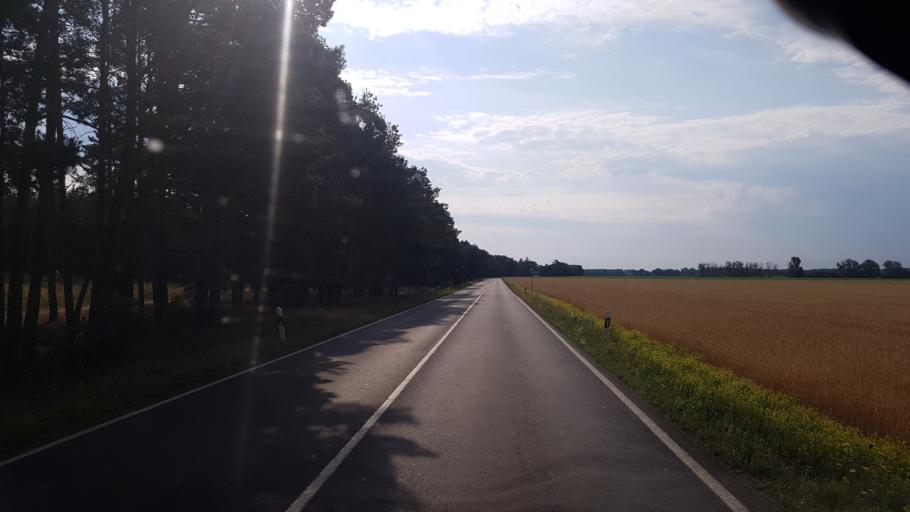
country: DE
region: Brandenburg
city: Baruth
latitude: 52.0579
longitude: 13.5570
